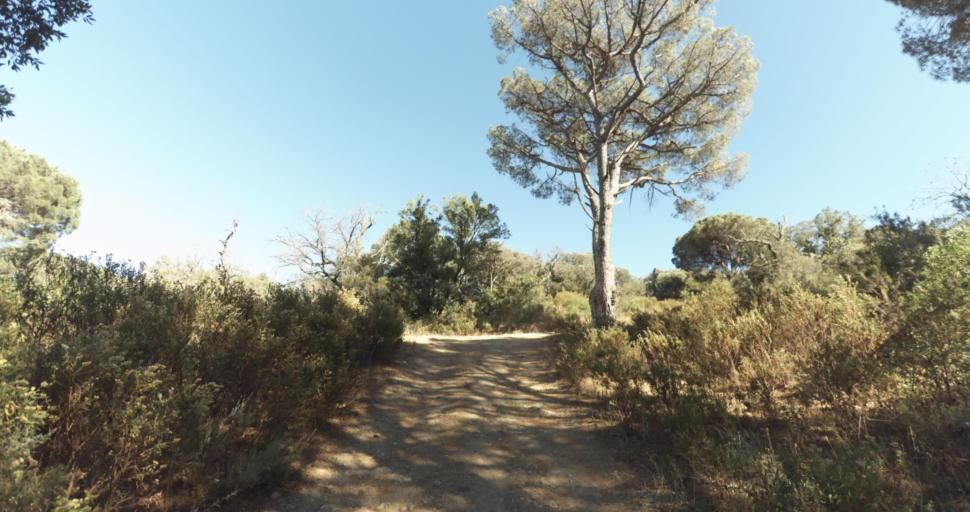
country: FR
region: Provence-Alpes-Cote d'Azur
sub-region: Departement du Var
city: Gassin
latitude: 43.2495
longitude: 6.5858
